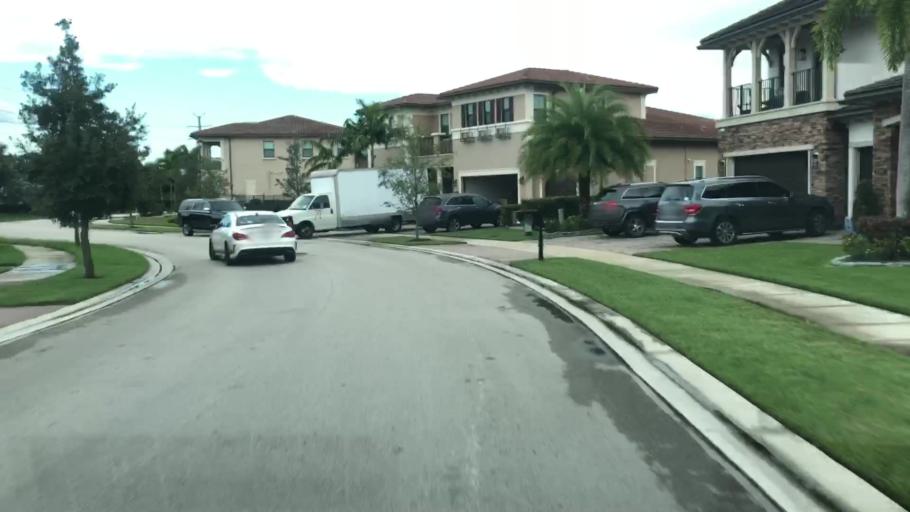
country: US
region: Florida
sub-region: Broward County
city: Parkland
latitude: 26.3419
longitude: -80.2759
